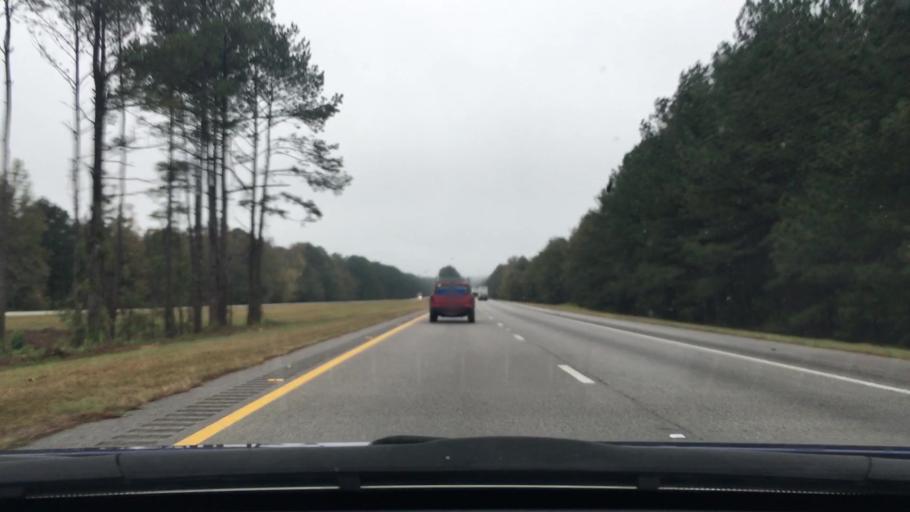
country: US
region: South Carolina
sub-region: Kershaw County
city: Camden
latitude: 34.2108
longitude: -80.4875
